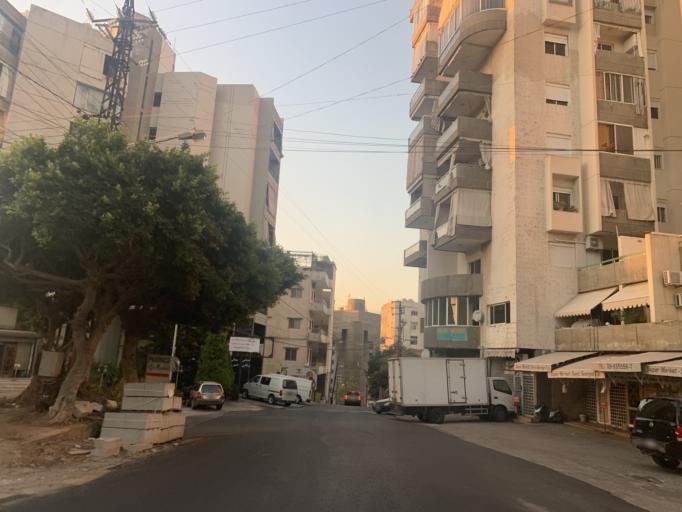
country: LB
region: Mont-Liban
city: Djounie
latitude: 33.9754
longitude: 35.6286
